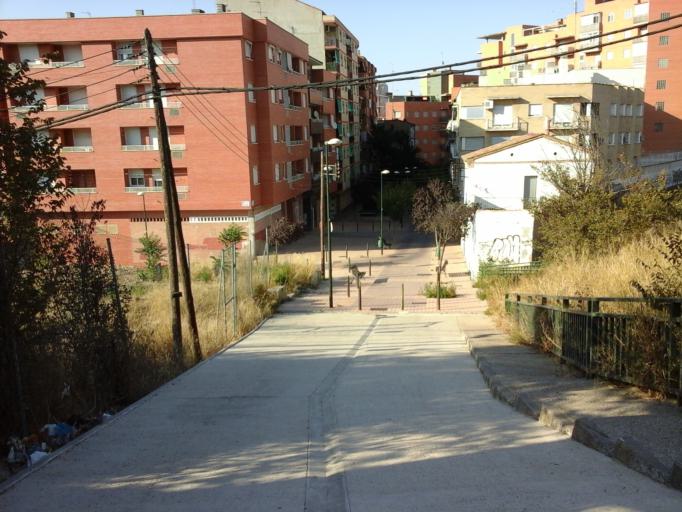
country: ES
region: Aragon
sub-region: Provincia de Zaragoza
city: Zaragoza
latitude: 41.6304
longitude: -0.8771
